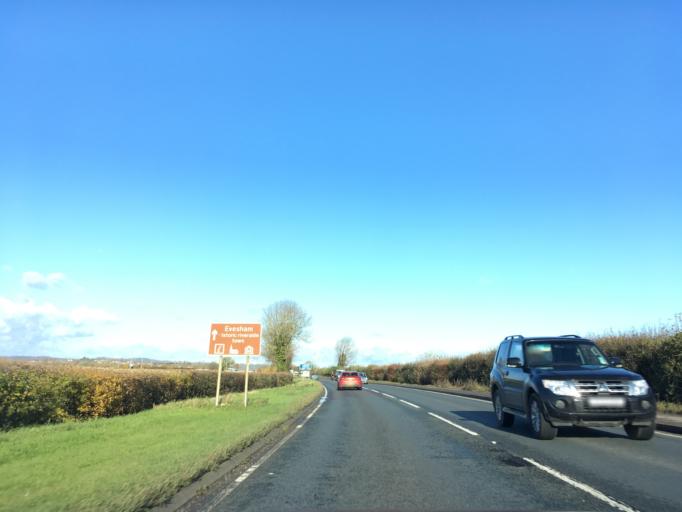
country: GB
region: England
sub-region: Worcestershire
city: Evesham
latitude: 52.0676
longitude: -1.9546
